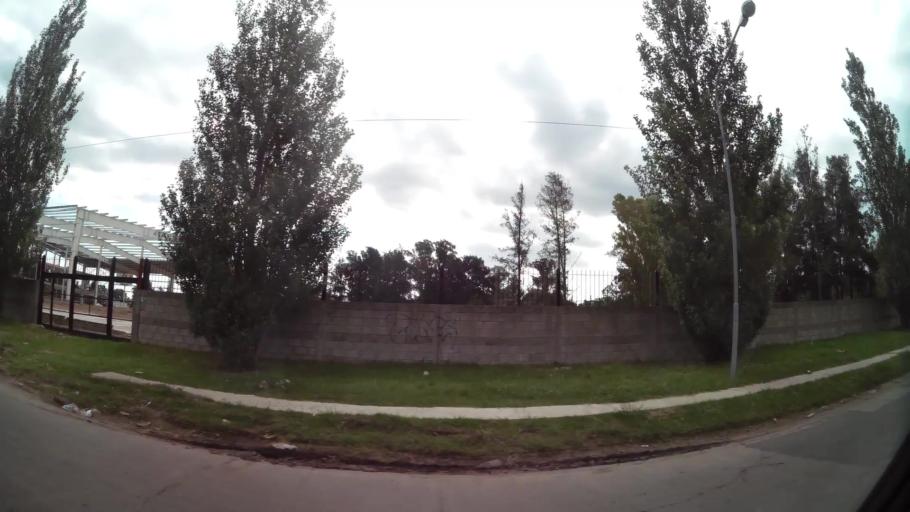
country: AR
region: Buenos Aires
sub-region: Partido de Tigre
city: Tigre
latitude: -34.4796
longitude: -58.6405
